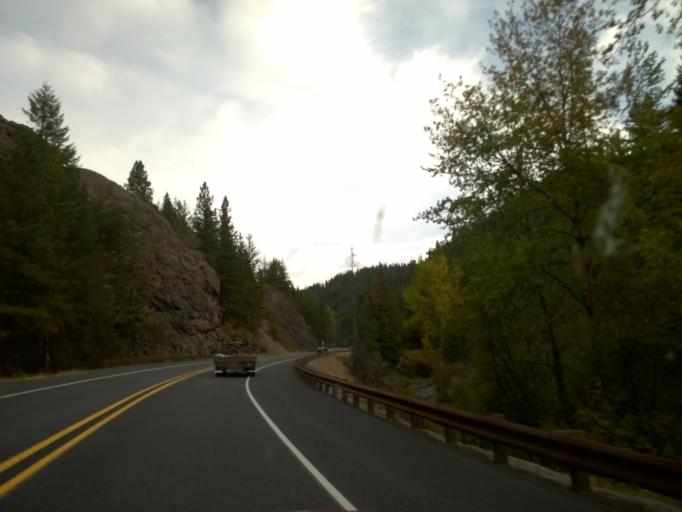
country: US
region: Washington
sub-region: Chelan County
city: Leavenworth
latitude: 47.4108
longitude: -120.6578
